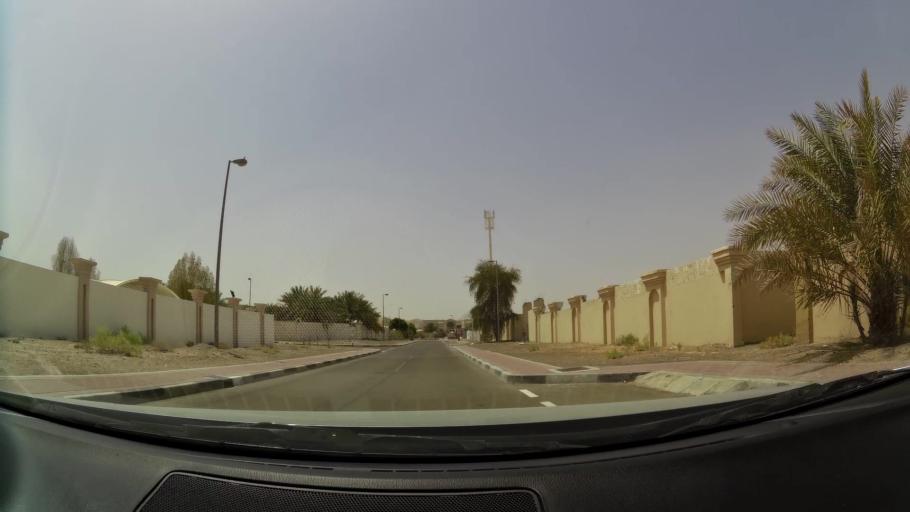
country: AE
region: Abu Dhabi
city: Al Ain
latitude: 24.1847
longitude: 55.7261
